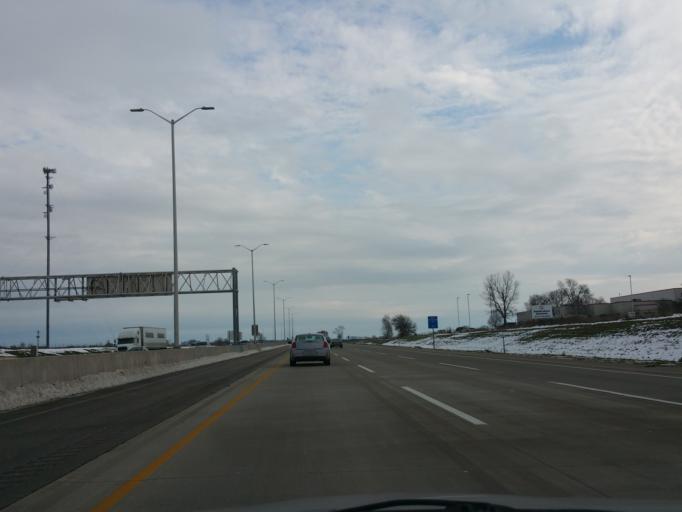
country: US
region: Illinois
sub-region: Winnebago County
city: Cherry Valley
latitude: 42.2393
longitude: -88.9171
